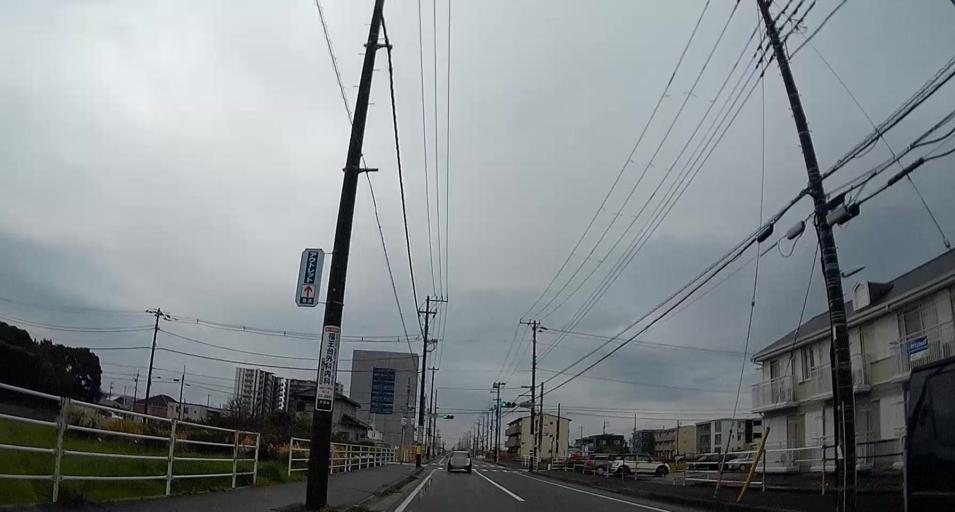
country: JP
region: Chiba
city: Kisarazu
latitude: 35.4348
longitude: 139.9598
